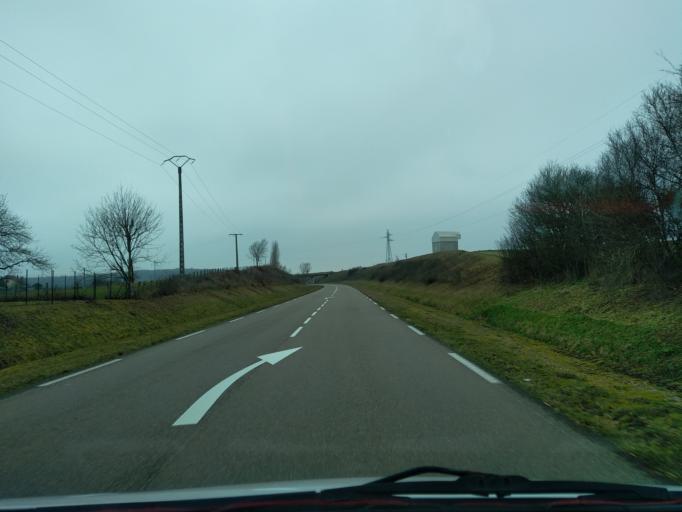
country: FR
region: Franche-Comte
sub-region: Departement de la Haute-Saone
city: Gray-la-Ville
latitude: 47.4052
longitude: 5.4778
